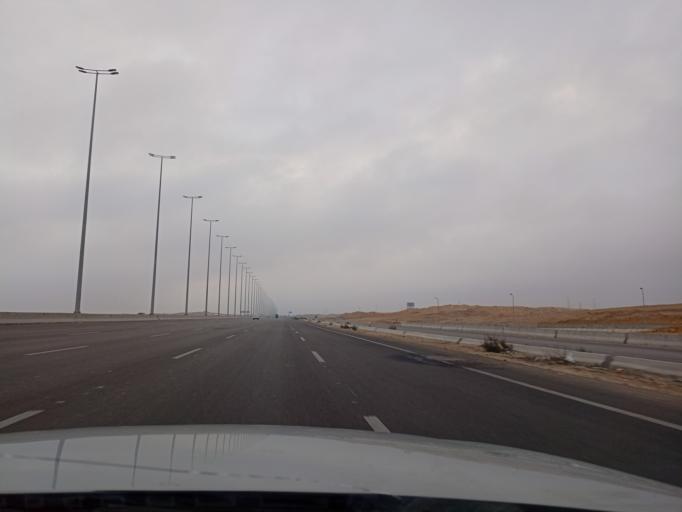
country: EG
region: Muhafazat al Qalyubiyah
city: Al Khankah
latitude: 30.0897
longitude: 31.5094
